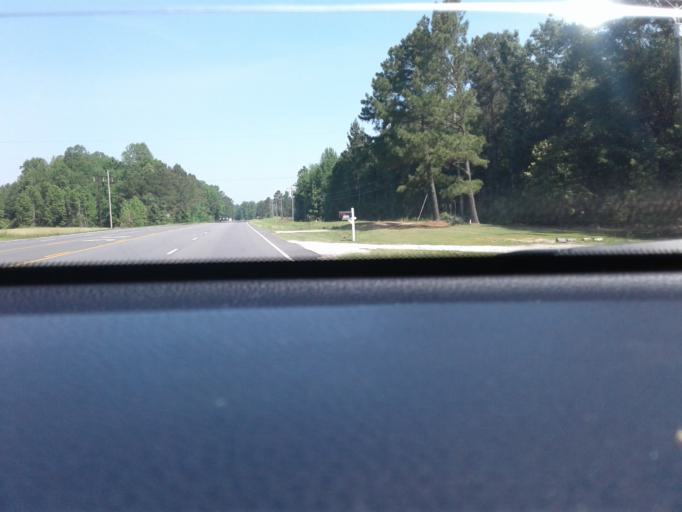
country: US
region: North Carolina
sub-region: Harnett County
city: Buies Creek
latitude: 35.3929
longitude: -78.7292
